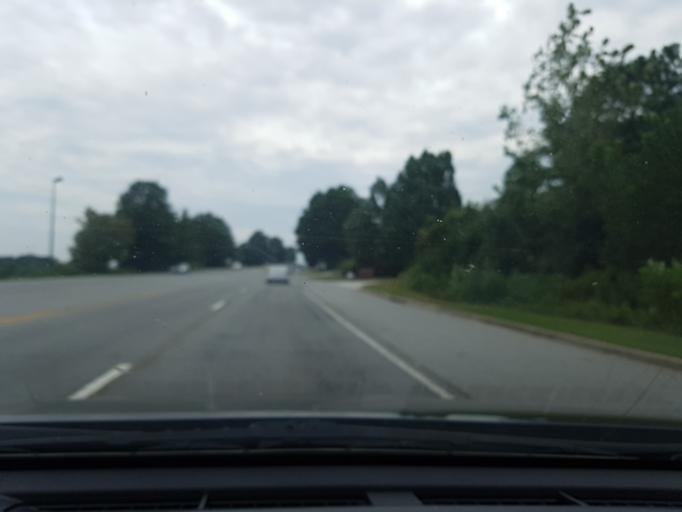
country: US
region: Georgia
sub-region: Gwinnett County
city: Duluth
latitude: 33.9726
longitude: -84.0951
